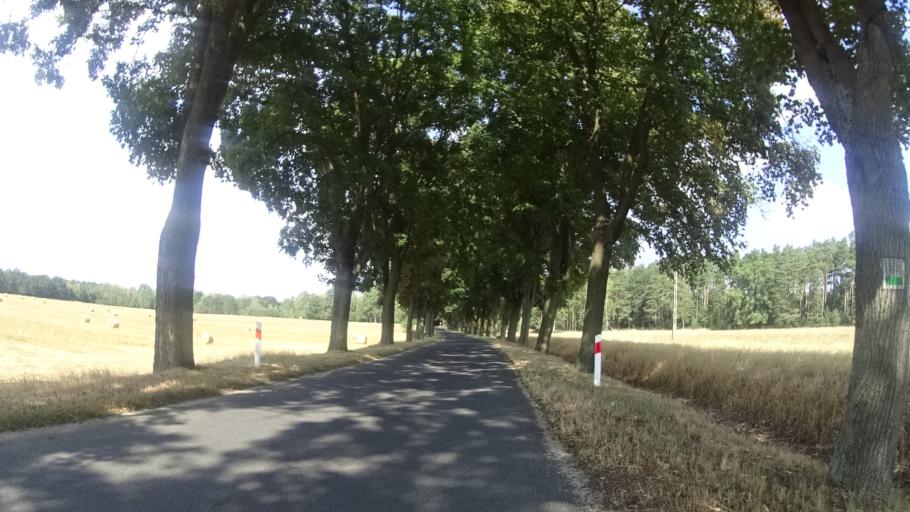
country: PL
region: Lubusz
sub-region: Powiat zarski
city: Przewoz
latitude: 51.5027
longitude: 14.8433
